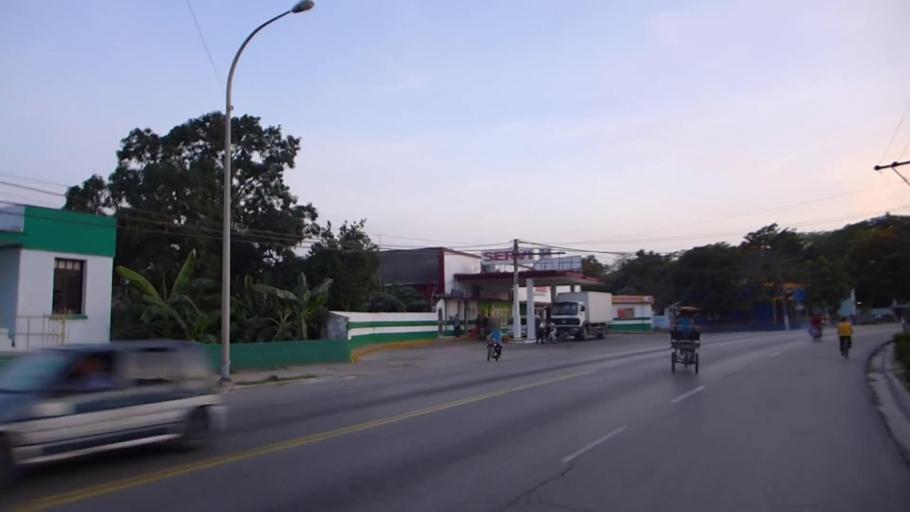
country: CU
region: Camaguey
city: Camaguey
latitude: 21.3745
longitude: -77.9158
